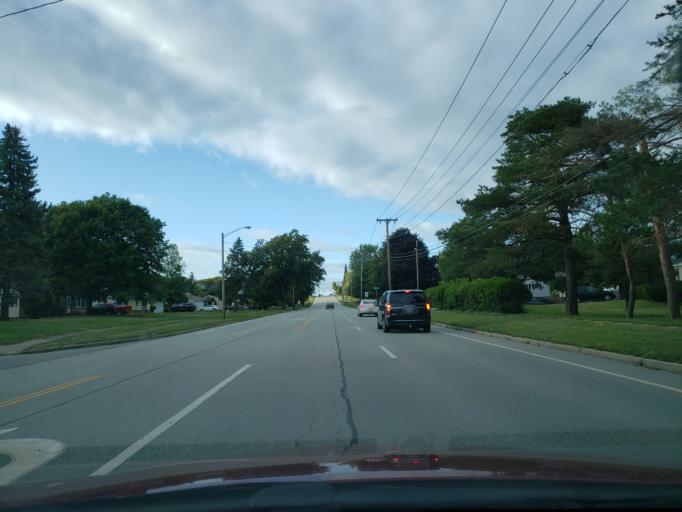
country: US
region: New York
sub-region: Monroe County
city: Greece
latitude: 43.2482
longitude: -77.6592
